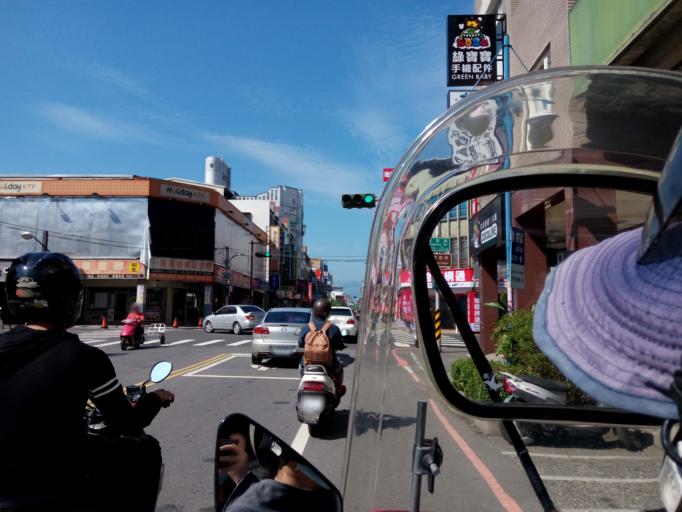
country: TW
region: Taiwan
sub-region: Yilan
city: Yilan
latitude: 24.6787
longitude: 121.7691
